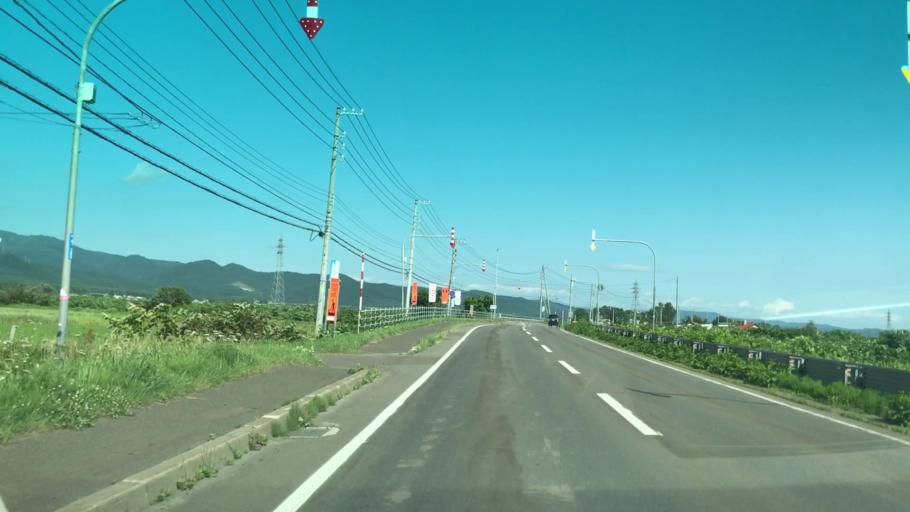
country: JP
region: Hokkaido
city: Iwanai
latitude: 43.0293
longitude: 140.5411
